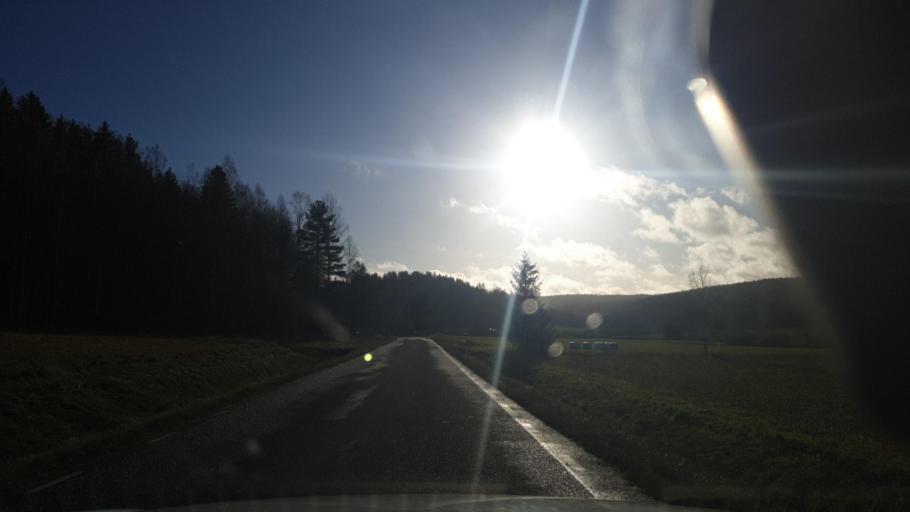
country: NO
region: Ostfold
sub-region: Romskog
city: Romskog
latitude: 59.7045
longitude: 12.0762
